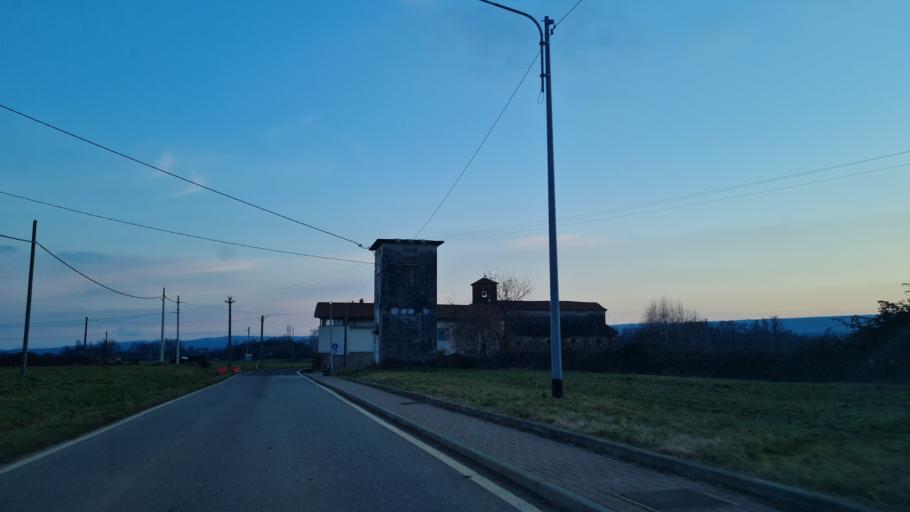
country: IT
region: Piedmont
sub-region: Provincia di Biella
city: Occhieppo Inferiore
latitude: 45.5439
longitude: 8.0249
